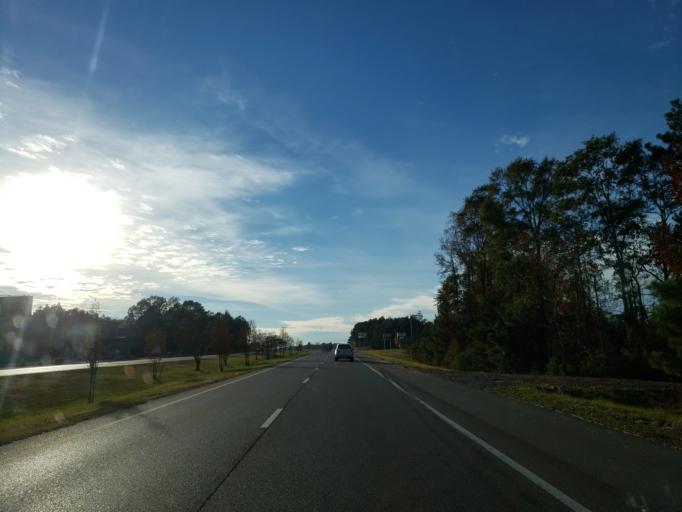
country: US
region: Mississippi
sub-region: Lamar County
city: West Hattiesburg
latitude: 31.3137
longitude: -89.4639
